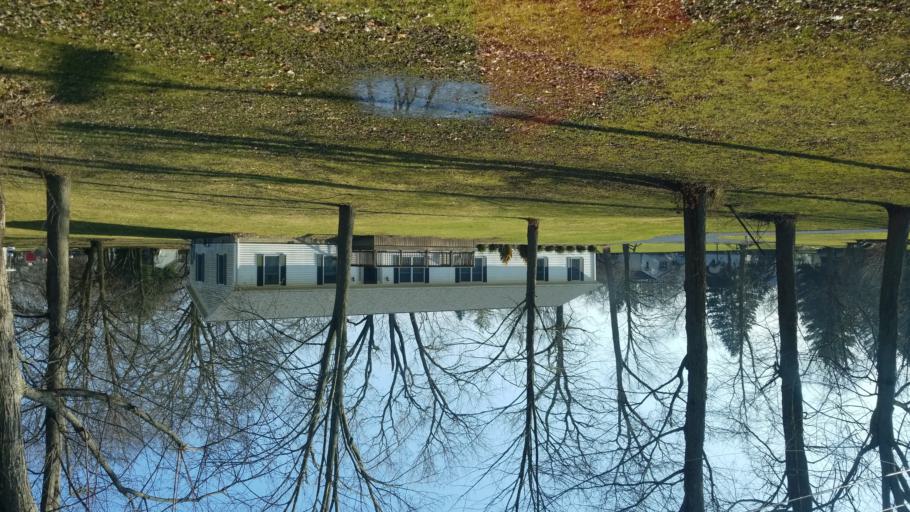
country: US
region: Ohio
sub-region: Seneca County
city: Tiffin
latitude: 41.1280
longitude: -83.1685
